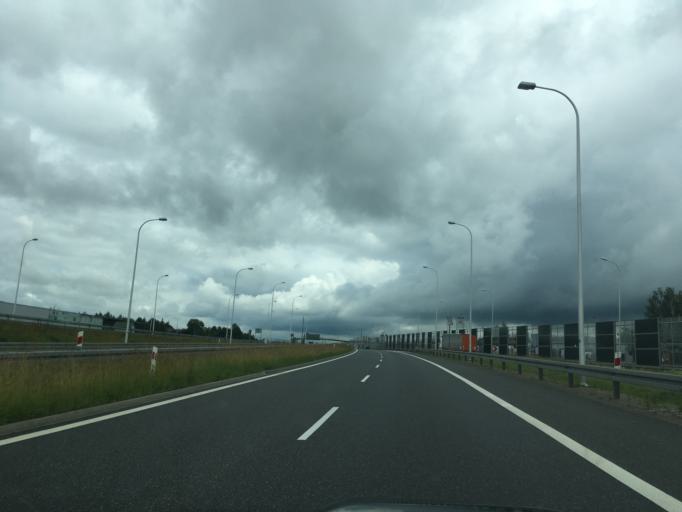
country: PL
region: Lublin Voivodeship
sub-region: Powiat swidnicki
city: Swidnik
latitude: 51.2064
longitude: 22.6602
